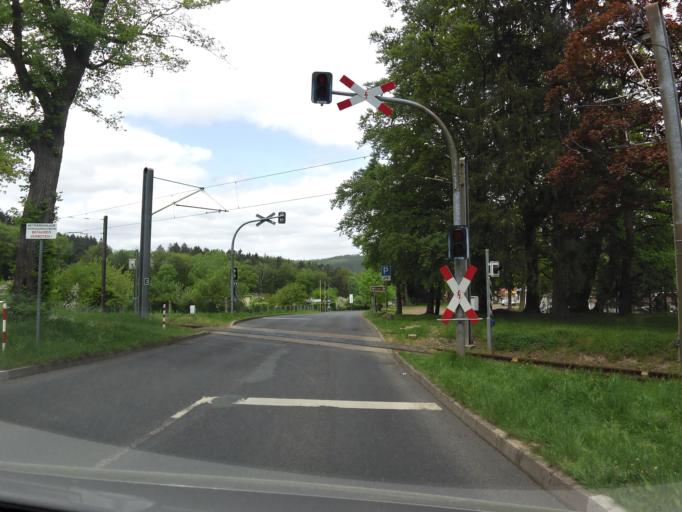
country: DE
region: Thuringia
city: Friedrichroda
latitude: 50.8589
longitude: 10.5566
